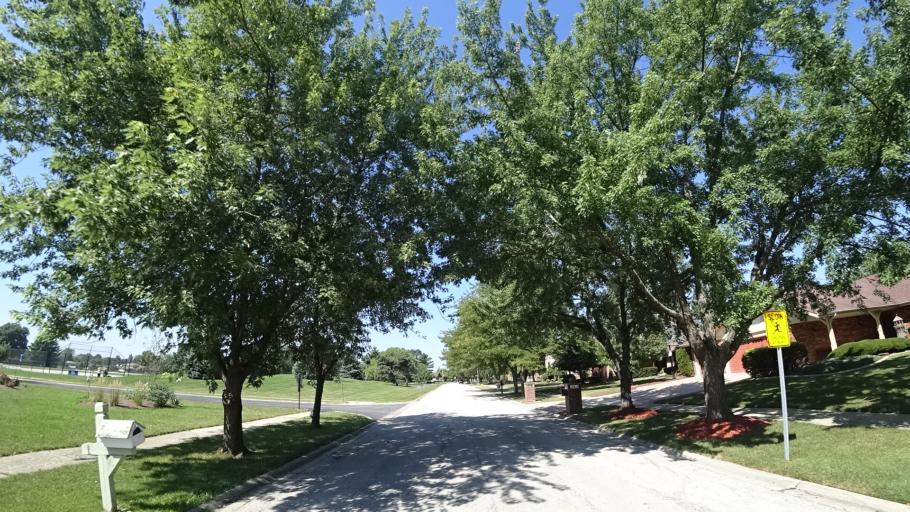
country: US
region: Illinois
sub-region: Cook County
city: Orland Park
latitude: 41.6346
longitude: -87.8218
